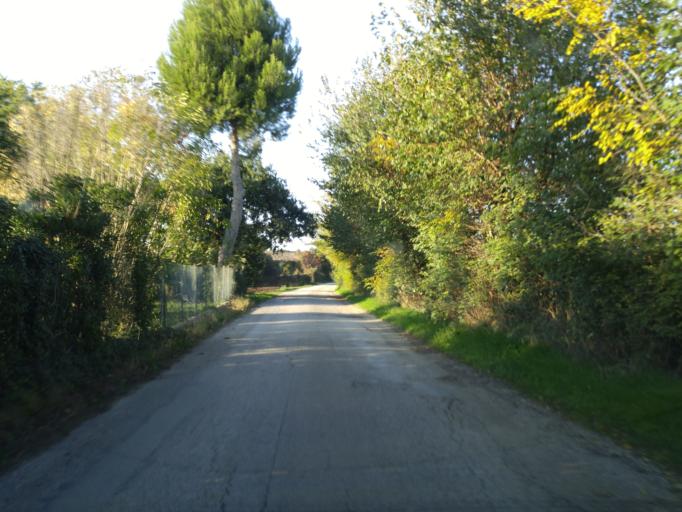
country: IT
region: The Marches
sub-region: Provincia di Pesaro e Urbino
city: Fano
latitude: 43.8149
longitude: 13.0318
